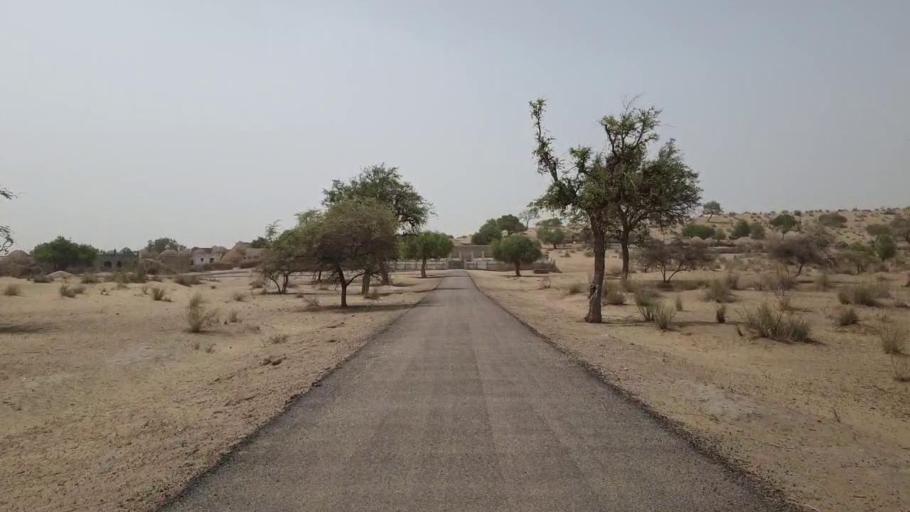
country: PK
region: Sindh
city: Islamkot
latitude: 24.7063
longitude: 70.6187
